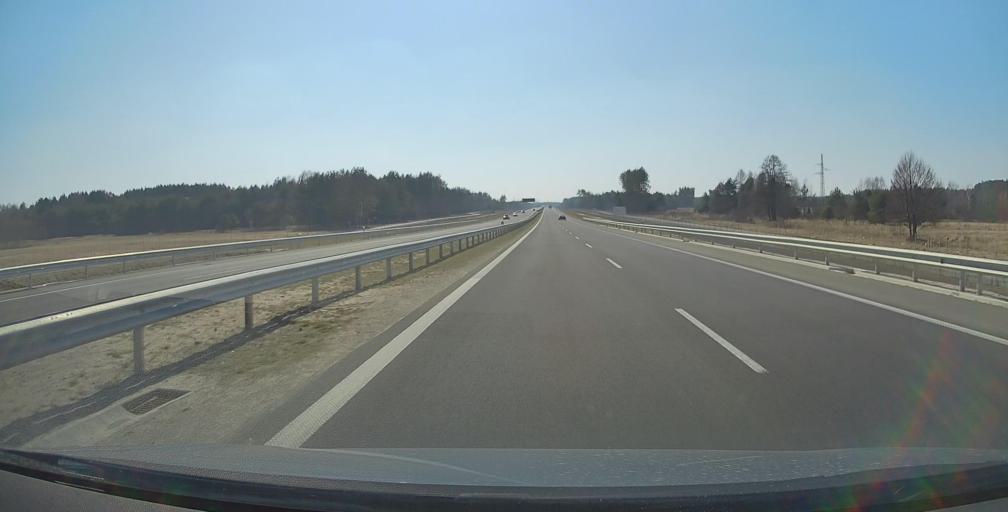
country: PL
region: Subcarpathian Voivodeship
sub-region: Powiat nizanski
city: Konczyce
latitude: 50.4599
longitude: 22.1409
